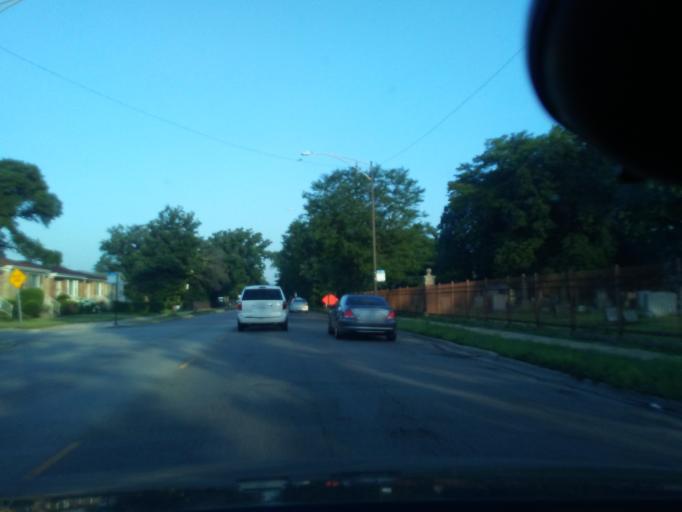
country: US
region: Illinois
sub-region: Cook County
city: Lincolnwood
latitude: 41.9757
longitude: -87.7194
